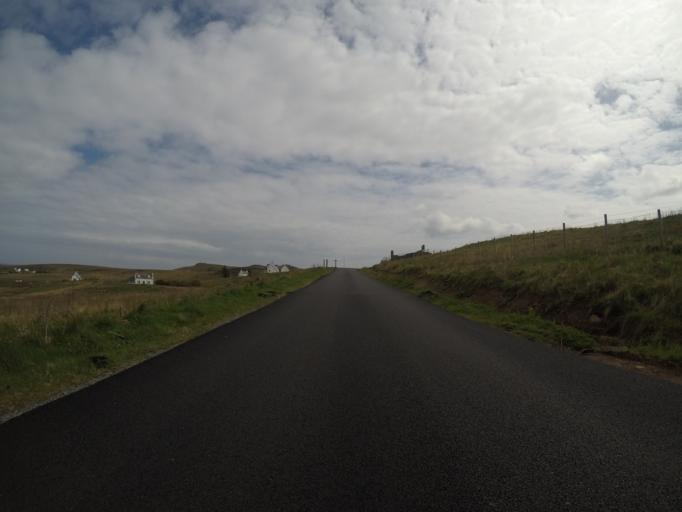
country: GB
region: Scotland
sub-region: Highland
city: Portree
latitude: 57.6824
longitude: -6.2974
